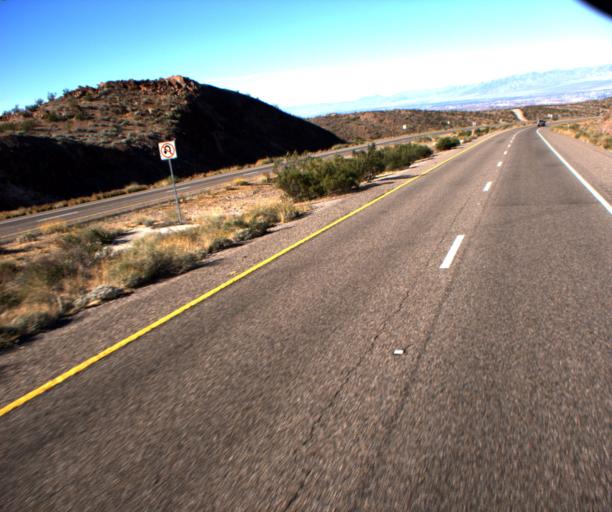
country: US
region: Nevada
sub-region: Clark County
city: Laughlin
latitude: 35.1876
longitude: -114.4505
